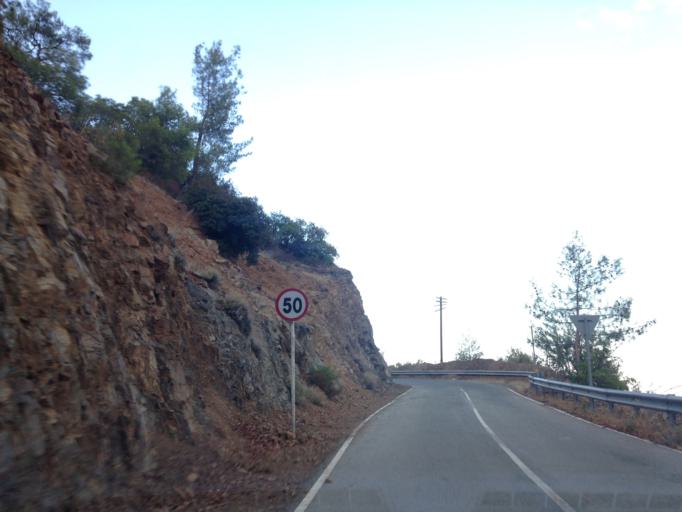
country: CY
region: Lefkosia
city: Lefka
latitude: 35.0091
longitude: 32.7302
